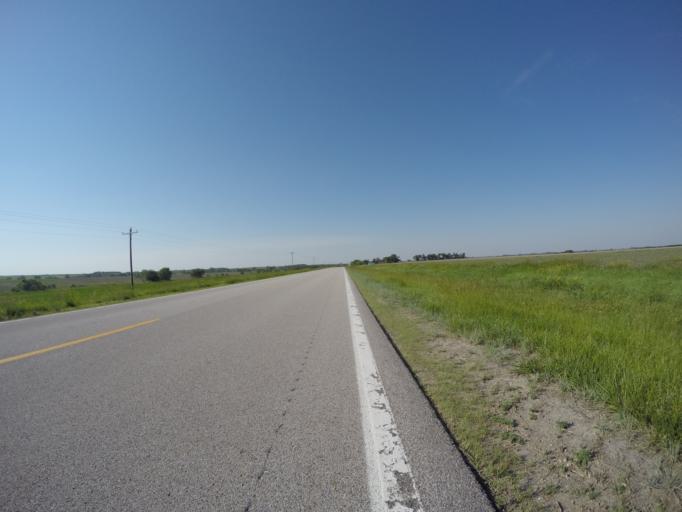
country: US
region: Nebraska
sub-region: Gage County
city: Wymore
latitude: 40.0534
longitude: -96.4829
